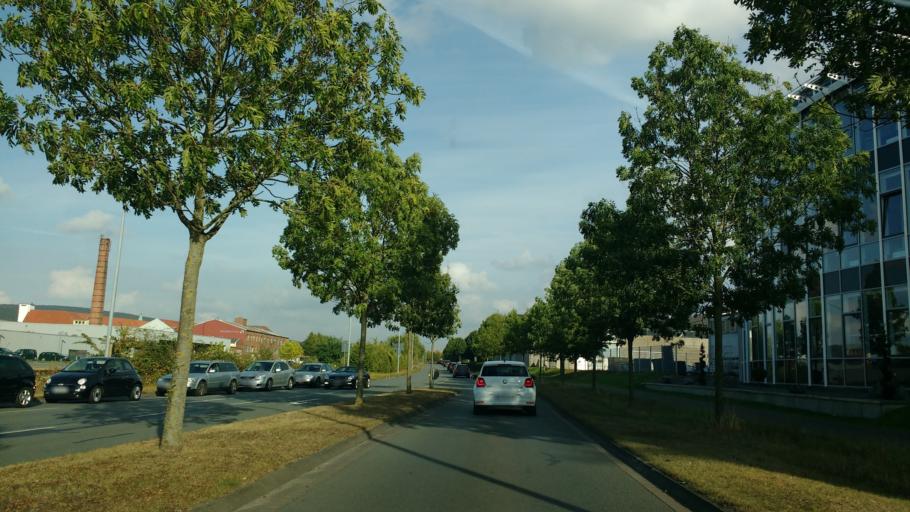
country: DE
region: North Rhine-Westphalia
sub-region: Regierungsbezirk Detmold
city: Lemgo
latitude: 52.0214
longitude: 8.8887
